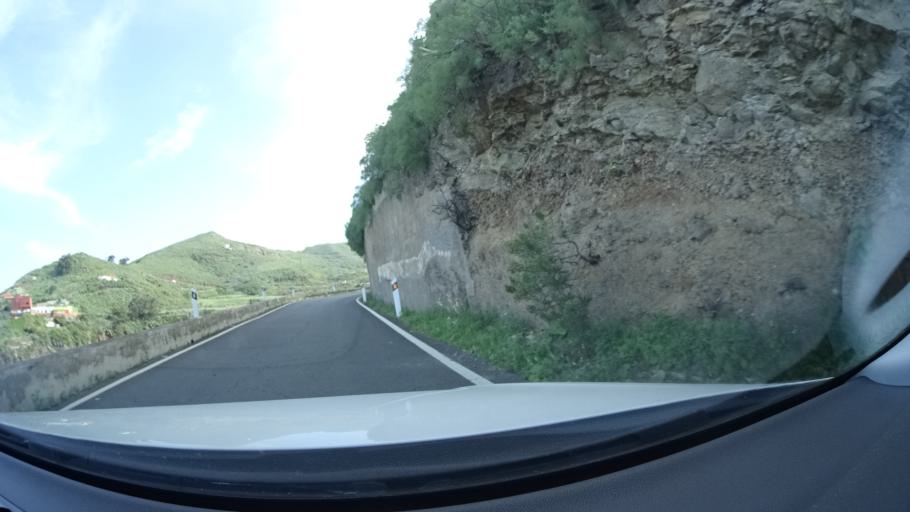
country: ES
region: Canary Islands
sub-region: Provincia de Las Palmas
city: Guia
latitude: 28.1136
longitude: -15.6415
